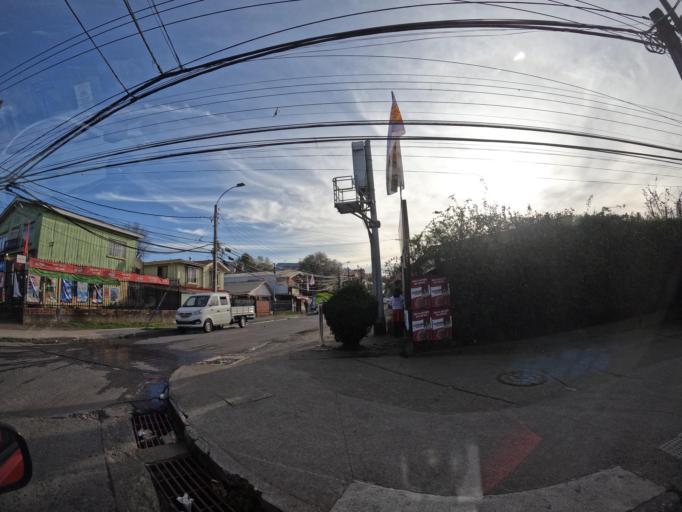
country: CL
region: Biobio
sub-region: Provincia de Concepcion
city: Concepcion
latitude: -36.7938
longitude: -73.0455
